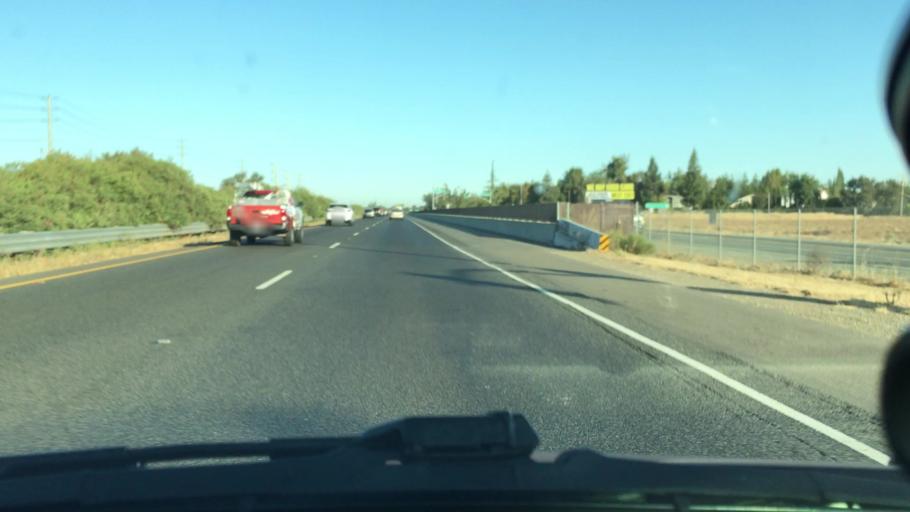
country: US
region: California
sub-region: Sacramento County
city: Elk Grove
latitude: 38.3847
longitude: -121.3700
